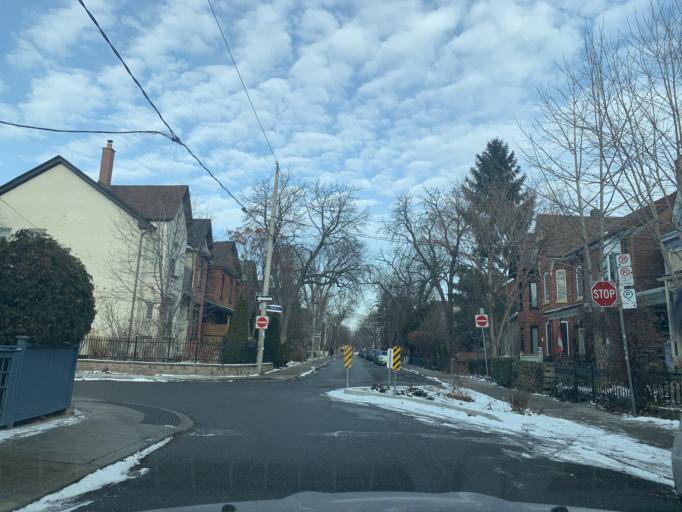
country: CA
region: Ontario
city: Toronto
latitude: 43.6606
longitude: -79.4044
